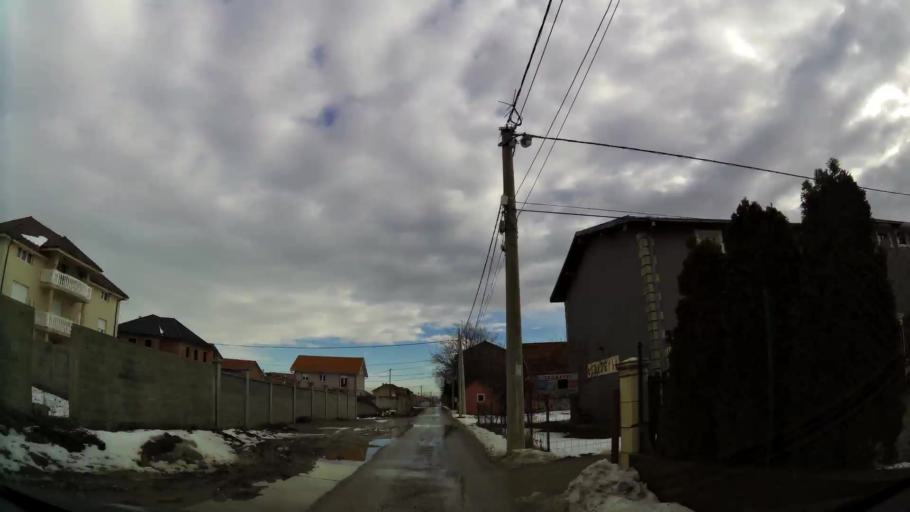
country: RS
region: Central Serbia
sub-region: Belgrade
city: Surcin
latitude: 44.8029
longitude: 20.3248
